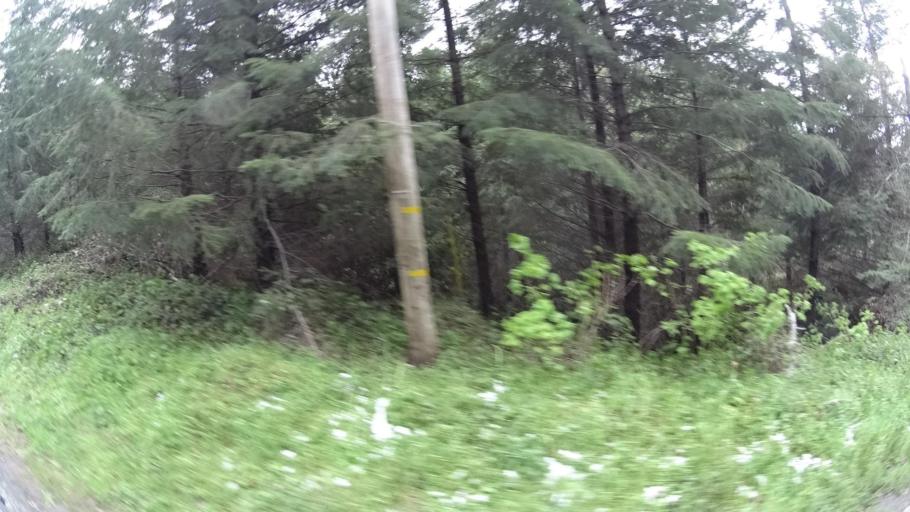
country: US
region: California
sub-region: Humboldt County
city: Blue Lake
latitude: 40.8646
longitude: -123.9096
